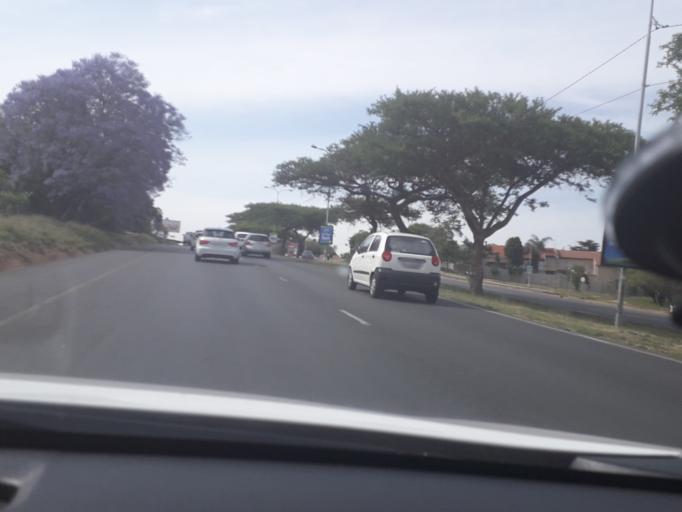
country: ZA
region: Gauteng
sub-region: City of Johannesburg Metropolitan Municipality
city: Midrand
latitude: -26.0662
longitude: 28.0249
